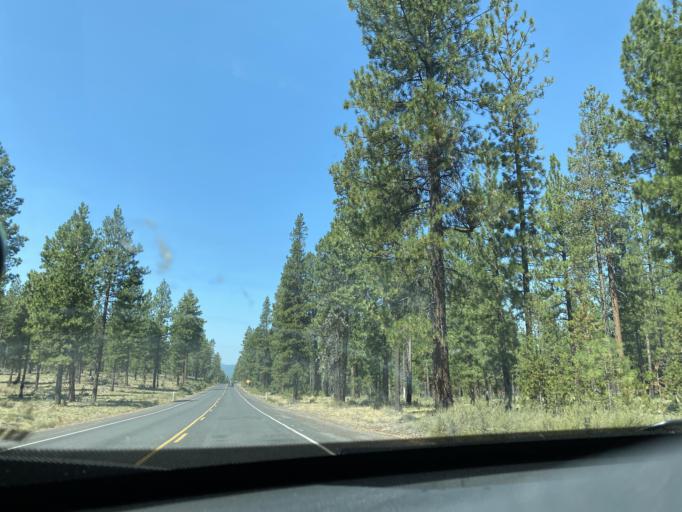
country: US
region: Oregon
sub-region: Deschutes County
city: Sunriver
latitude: 43.8911
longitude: -121.4046
